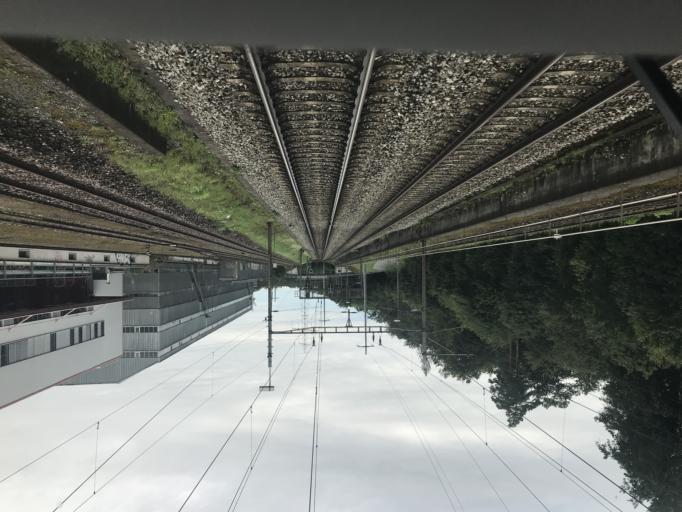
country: CH
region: Zurich
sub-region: Bezirk Buelach
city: Buelach / Soligaenter
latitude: 47.5302
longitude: 8.5277
